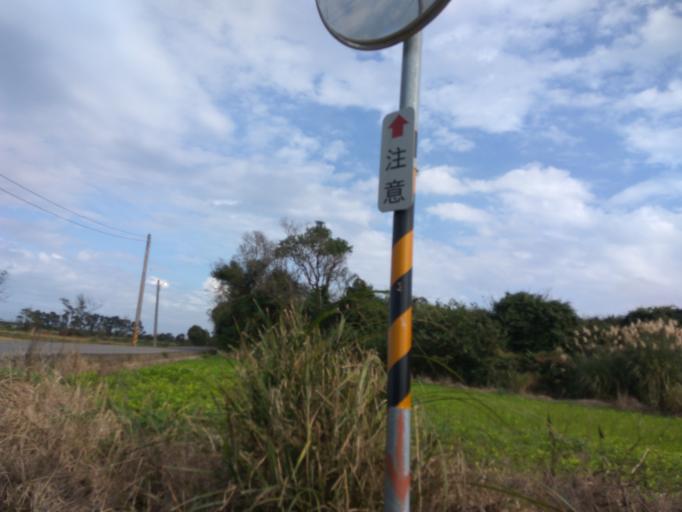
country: TW
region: Taiwan
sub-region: Hsinchu
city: Zhubei
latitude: 24.9498
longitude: 121.0053
